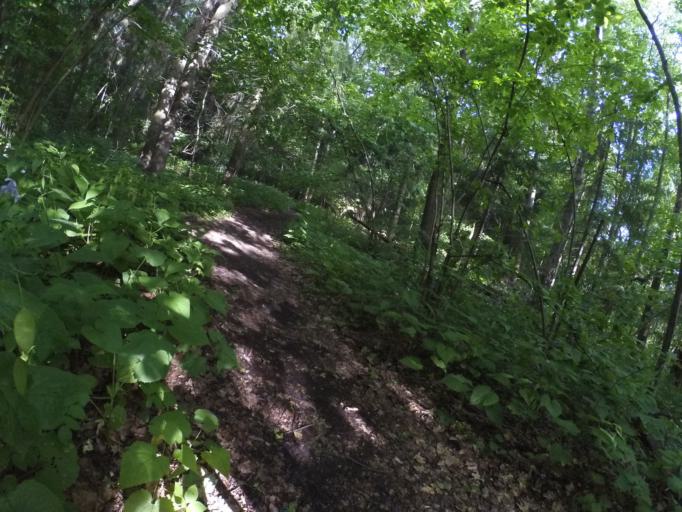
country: RU
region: Moscow
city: Ostankinskiy
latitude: 55.8403
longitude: 37.6113
